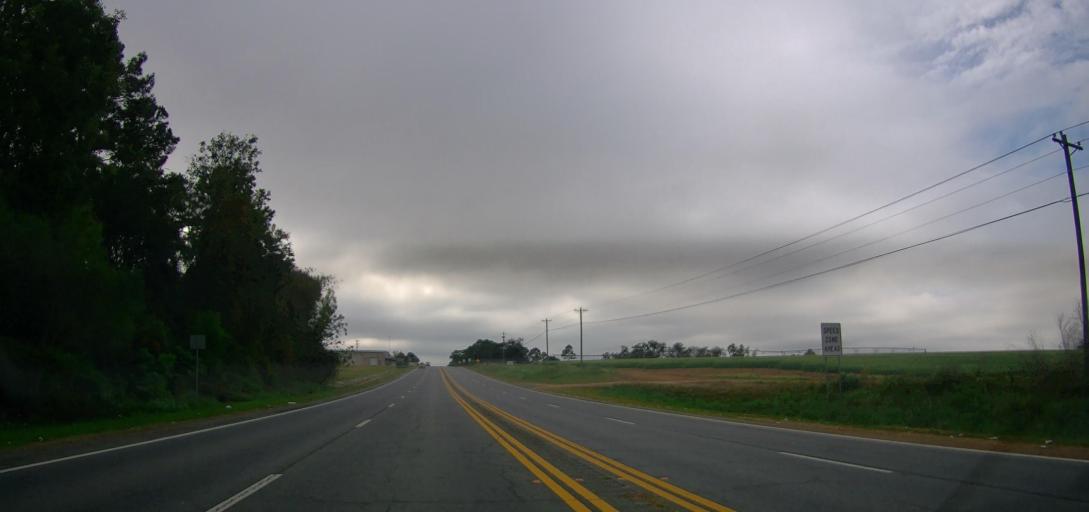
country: US
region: Georgia
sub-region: Tift County
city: Omega
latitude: 31.3499
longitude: -83.5862
